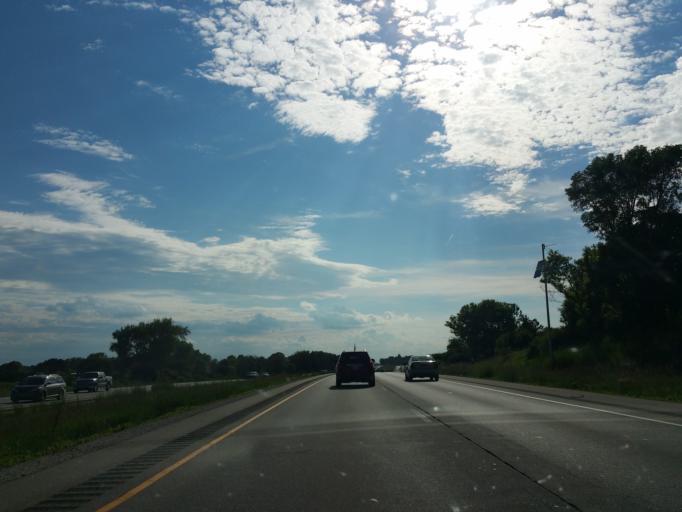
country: US
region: Wisconsin
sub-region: Jefferson County
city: Ixonia
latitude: 43.0852
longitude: -88.6233
